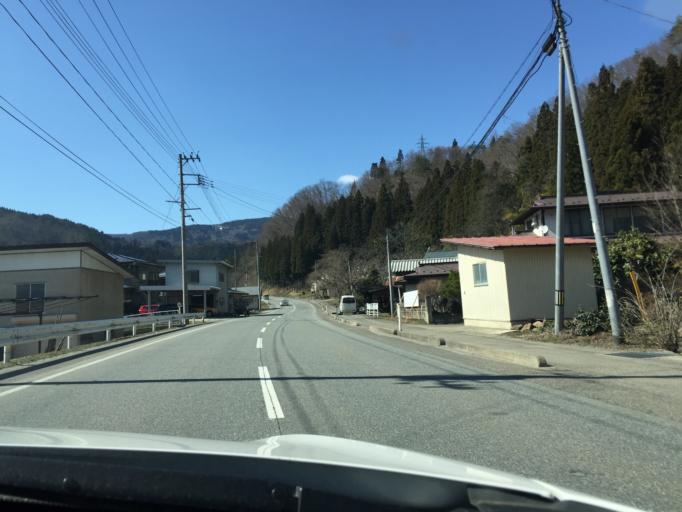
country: JP
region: Yamagata
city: Nagai
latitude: 38.2270
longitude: 140.0959
